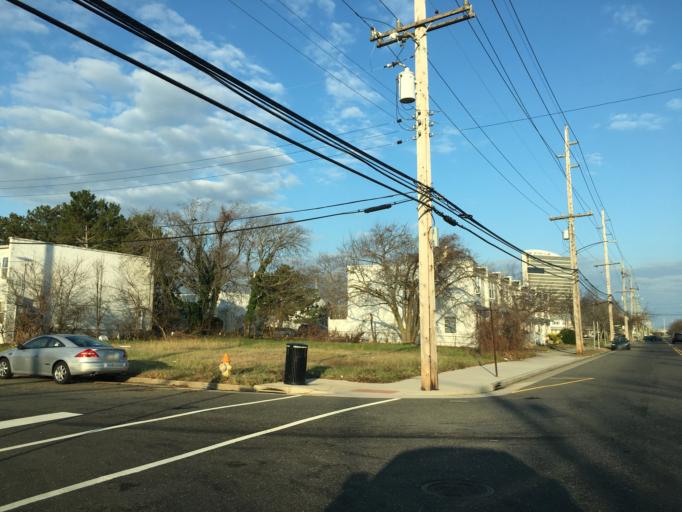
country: US
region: New Jersey
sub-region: Atlantic County
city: Atlantic City
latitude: 39.3714
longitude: -74.4263
